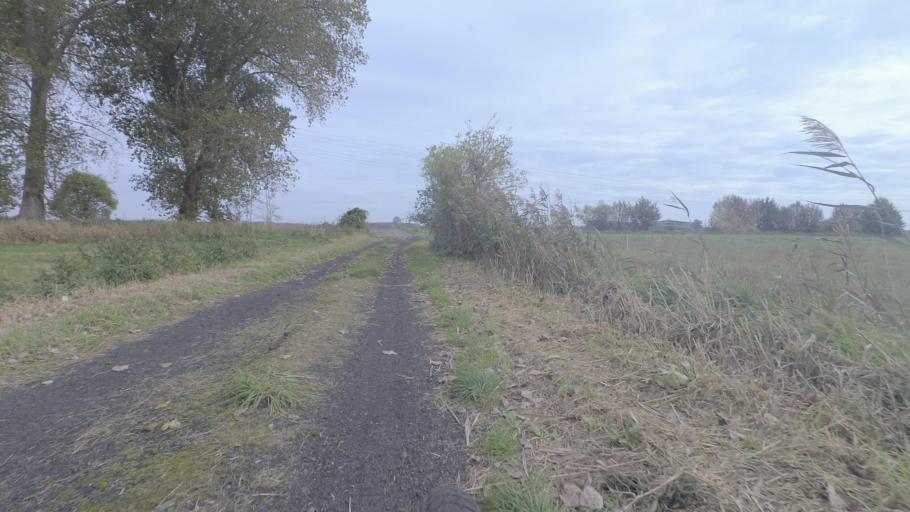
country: DE
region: Brandenburg
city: Grossbeeren
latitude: 52.3041
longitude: 13.3356
